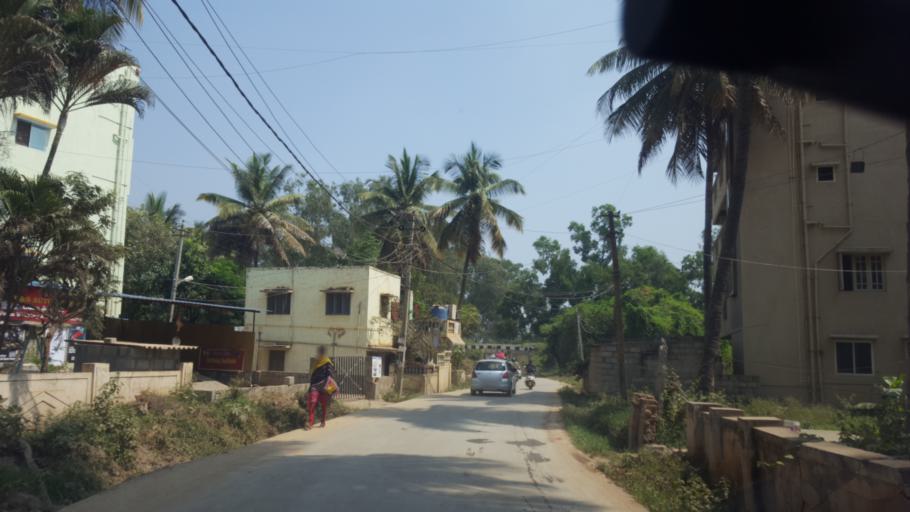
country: IN
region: Karnataka
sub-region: Bangalore Urban
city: Bangalore
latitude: 12.9357
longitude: 77.7063
